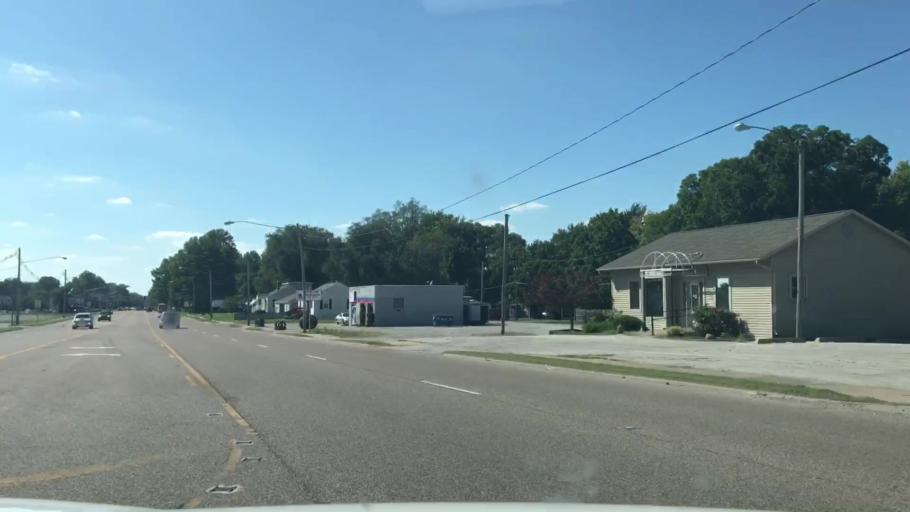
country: US
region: Illinois
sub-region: Saint Clair County
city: Swansea
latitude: 38.5416
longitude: -90.0298
